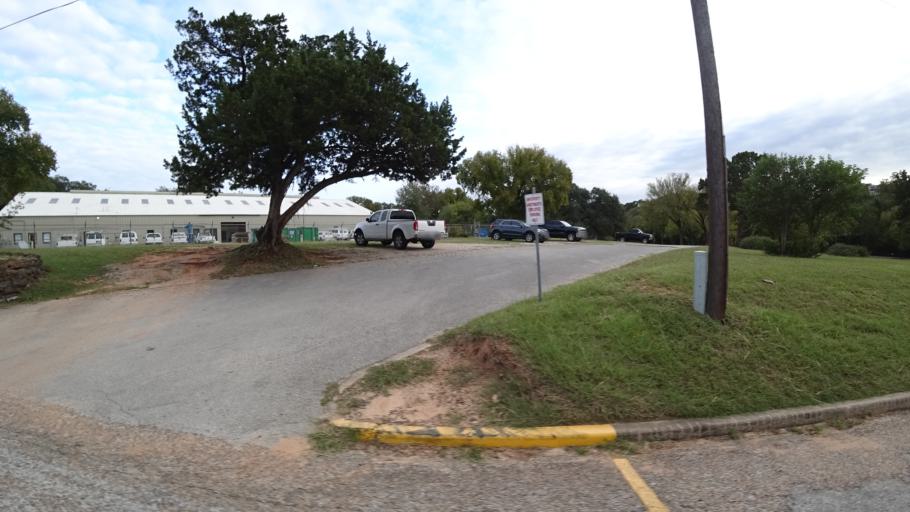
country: US
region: Texas
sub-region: Travis County
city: Rollingwood
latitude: 30.2871
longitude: -97.7829
